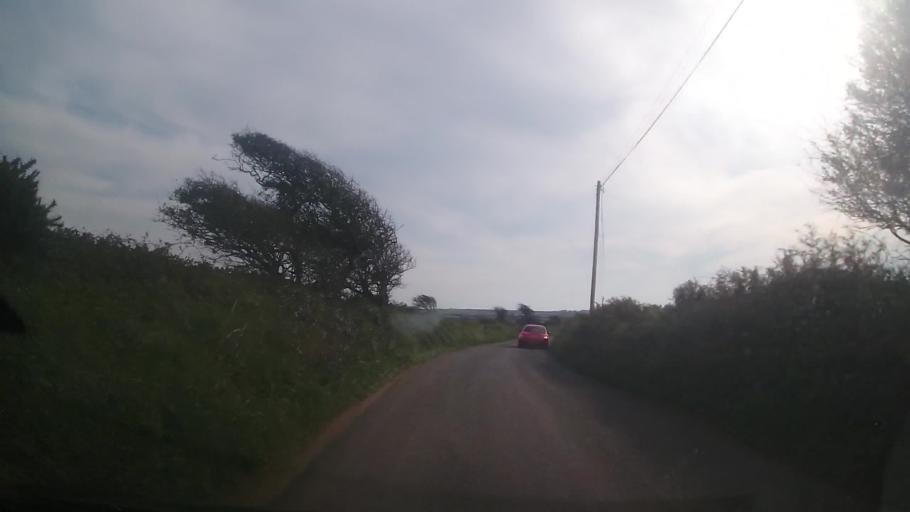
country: GB
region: Wales
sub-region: Pembrokeshire
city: Saint David's
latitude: 51.9066
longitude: -5.2424
